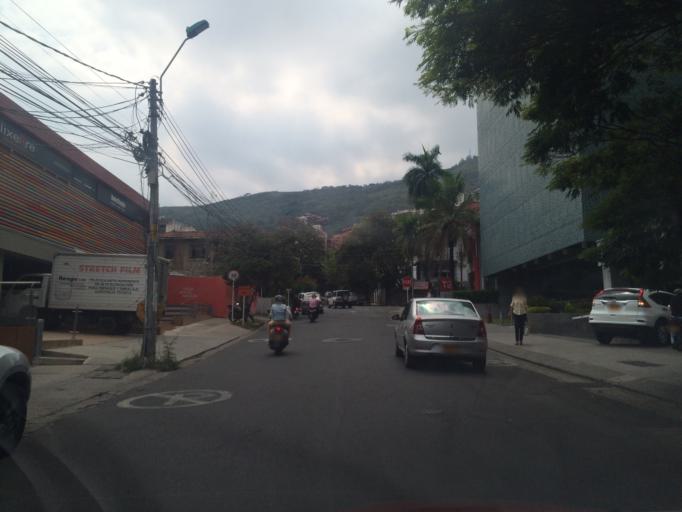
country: CO
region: Valle del Cauca
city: Cali
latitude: 3.4639
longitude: -76.5313
